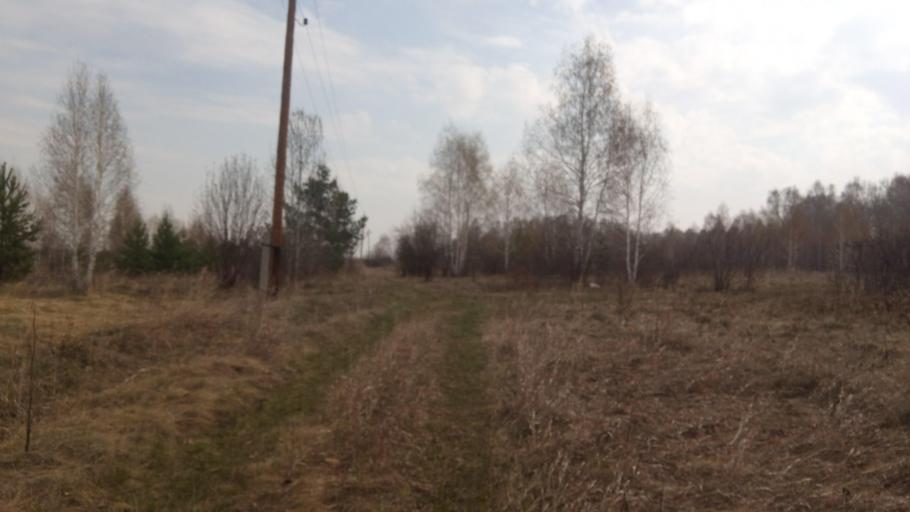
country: RU
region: Chelyabinsk
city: Timiryazevskiy
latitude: 54.9964
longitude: 60.8515
